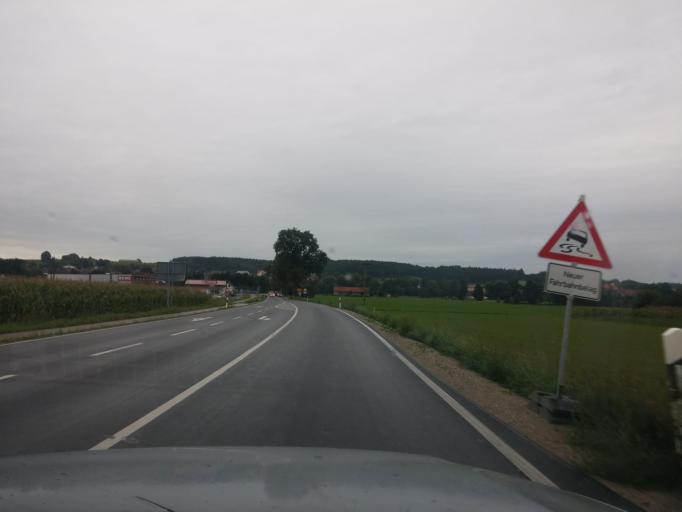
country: DE
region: Bavaria
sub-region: Upper Bavaria
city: Hohenkammer
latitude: 48.4317
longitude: 11.5225
